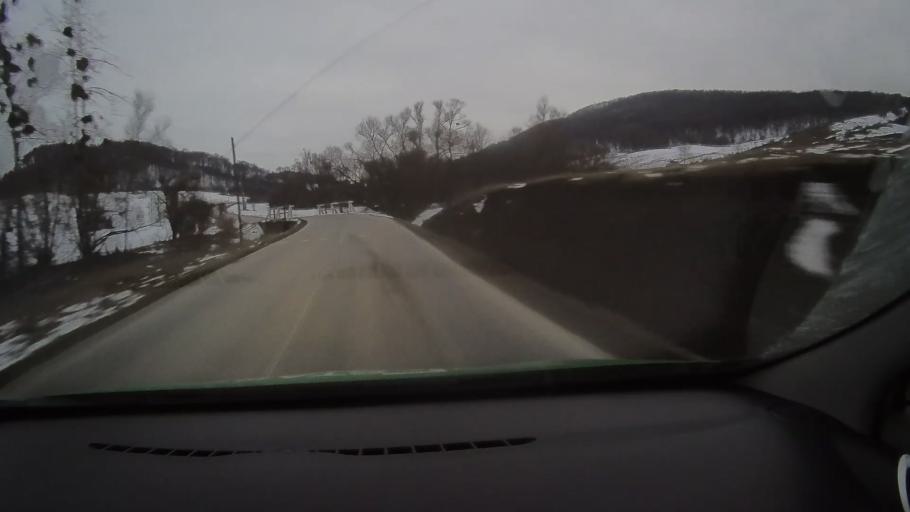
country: RO
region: Harghita
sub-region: Comuna Mugeni
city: Mugeni
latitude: 46.2280
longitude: 25.2384
